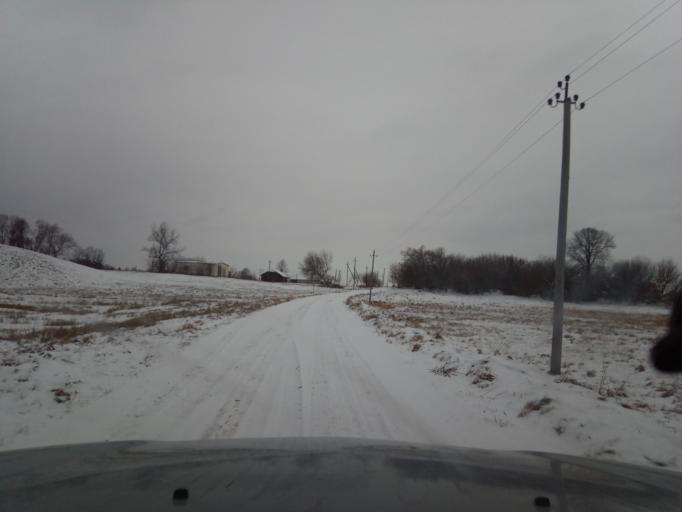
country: LT
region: Vilnius County
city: Ukmerge
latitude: 55.4788
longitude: 24.6232
